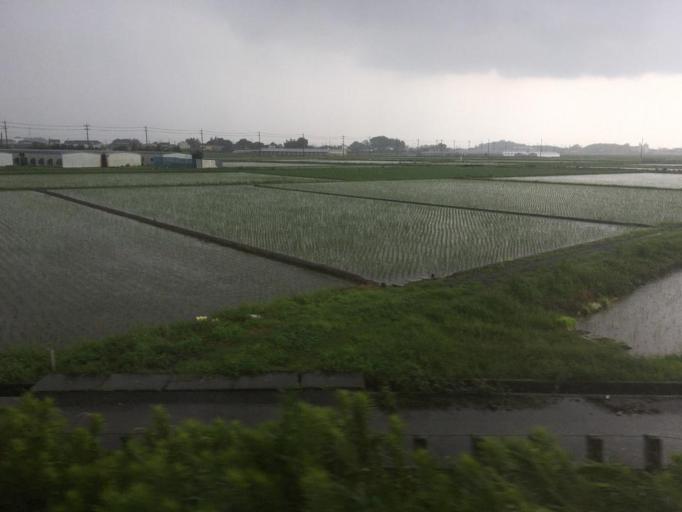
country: JP
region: Gunma
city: Tatebayashi
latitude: 36.2821
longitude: 139.4865
